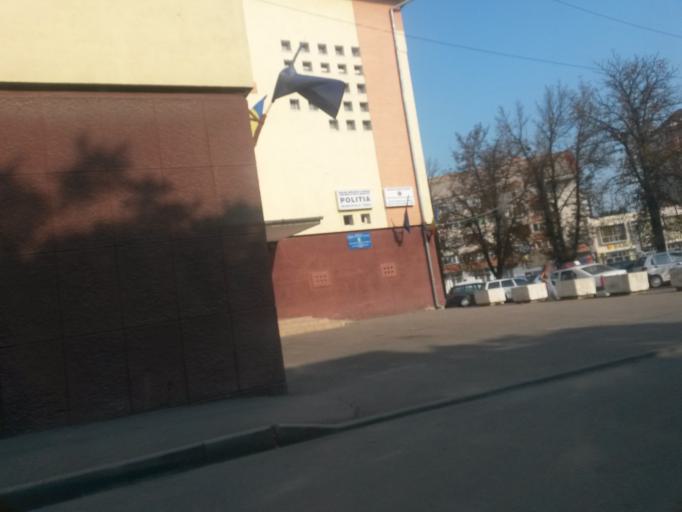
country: RO
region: Cluj
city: Turda
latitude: 46.5661
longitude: 23.7800
